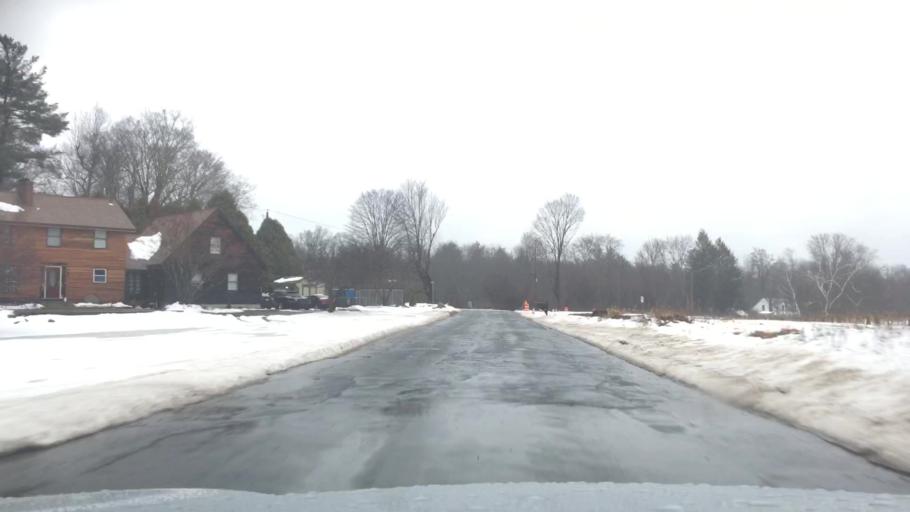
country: US
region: Massachusetts
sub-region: Hampshire County
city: Belchertown
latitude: 42.2776
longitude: -72.4383
